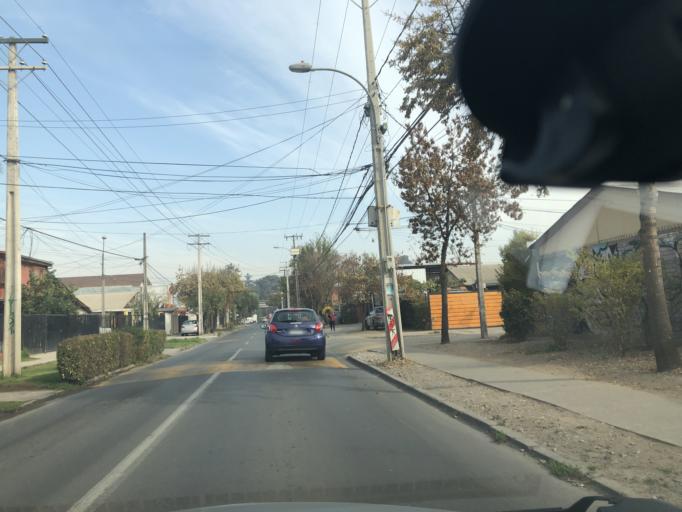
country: CL
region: Santiago Metropolitan
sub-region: Provincia de Cordillera
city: Puente Alto
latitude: -33.5804
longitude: -70.5783
